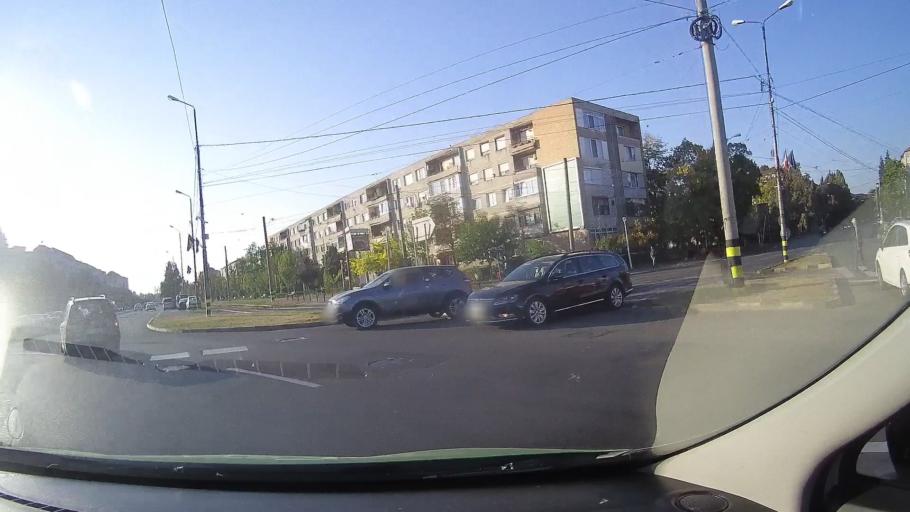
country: RO
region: Bihor
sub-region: Comuna Biharea
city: Oradea
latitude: 47.0736
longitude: 21.9146
